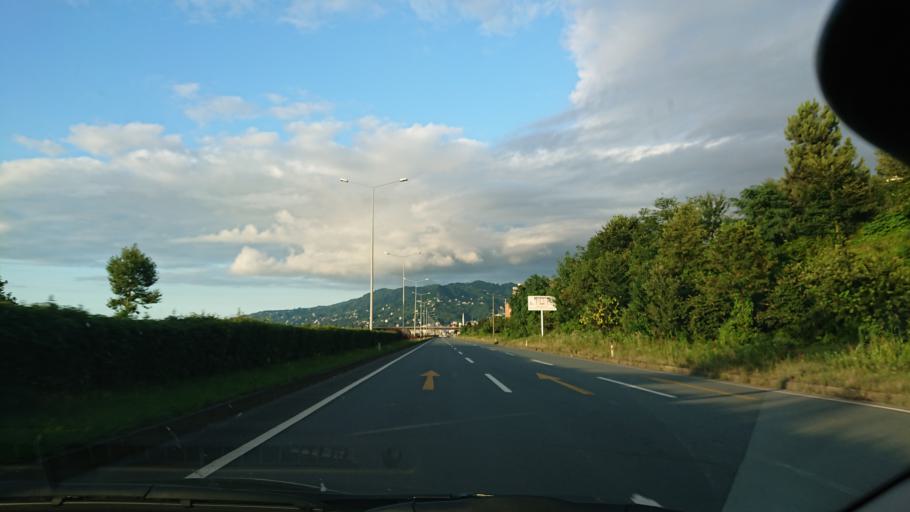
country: TR
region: Rize
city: Cayeli
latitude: 41.0795
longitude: 40.6986
